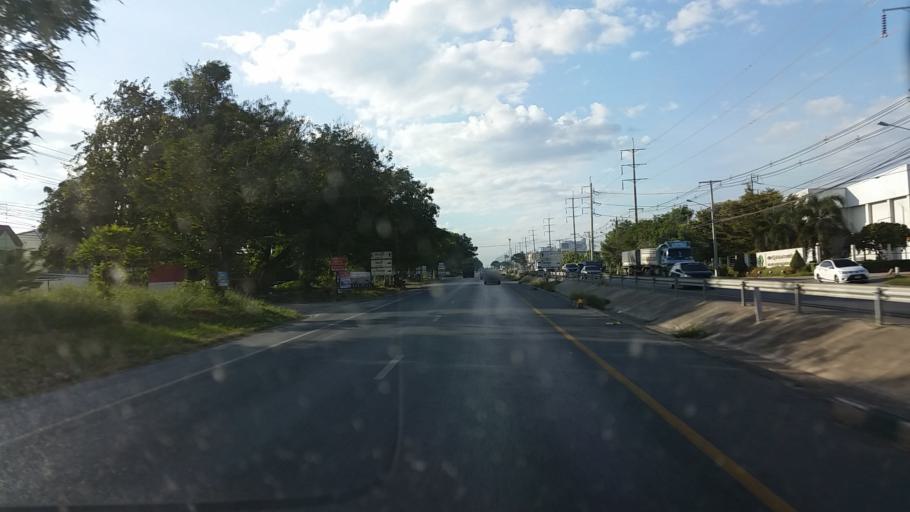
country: TH
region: Lop Buri
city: Phatthana Nikhom
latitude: 14.8296
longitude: 100.9107
